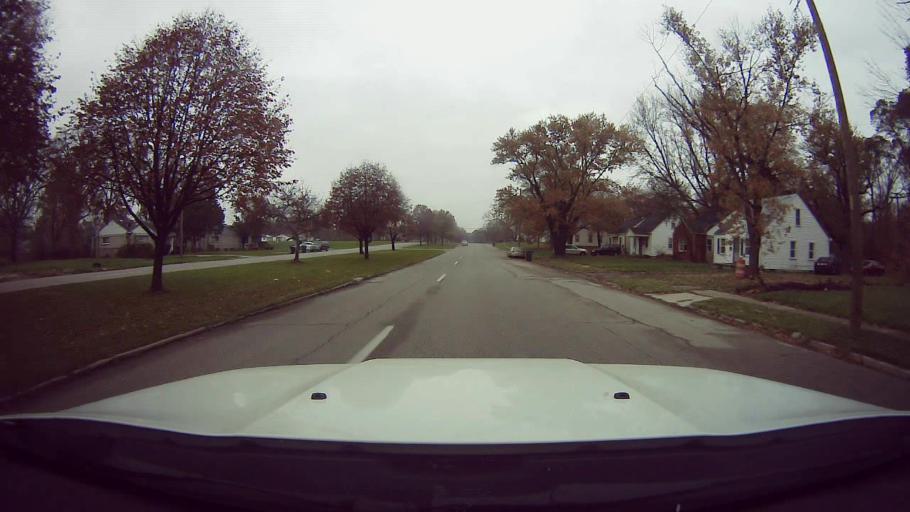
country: US
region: Michigan
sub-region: Wayne County
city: Redford
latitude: 42.3978
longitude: -83.2521
